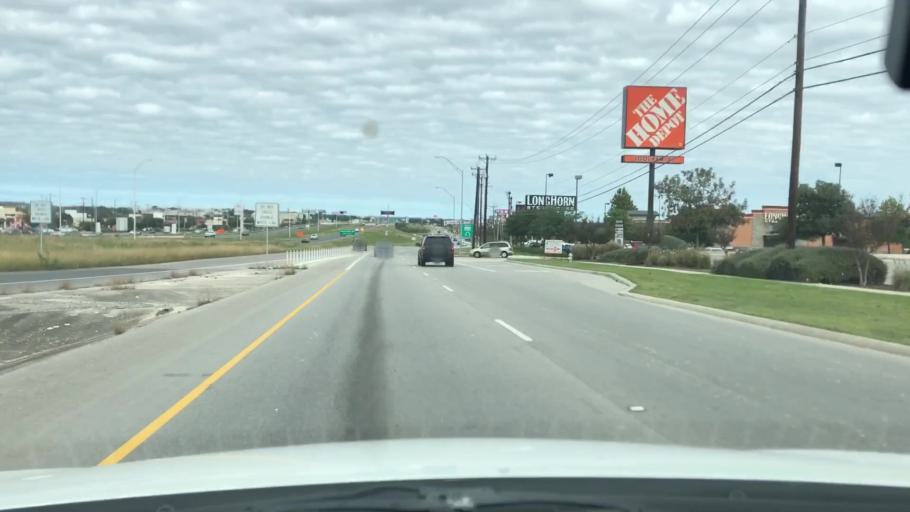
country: US
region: Texas
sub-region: Bexar County
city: Leon Valley
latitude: 29.4885
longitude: -98.7071
